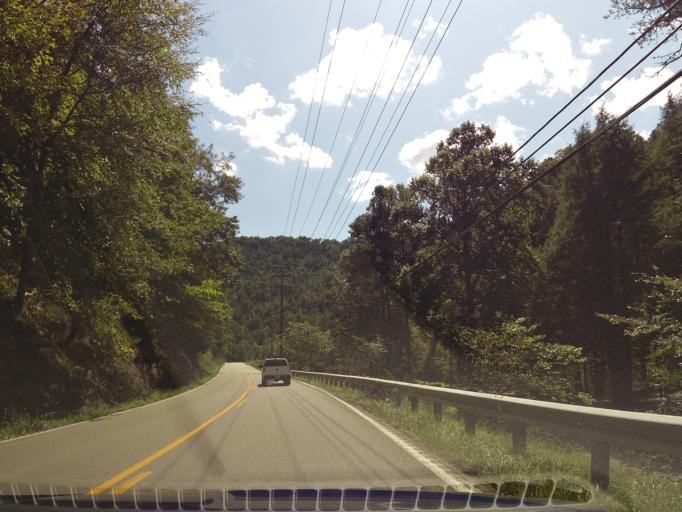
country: US
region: Kentucky
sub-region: Leslie County
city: Hyden
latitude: 37.0503
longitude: -83.4004
